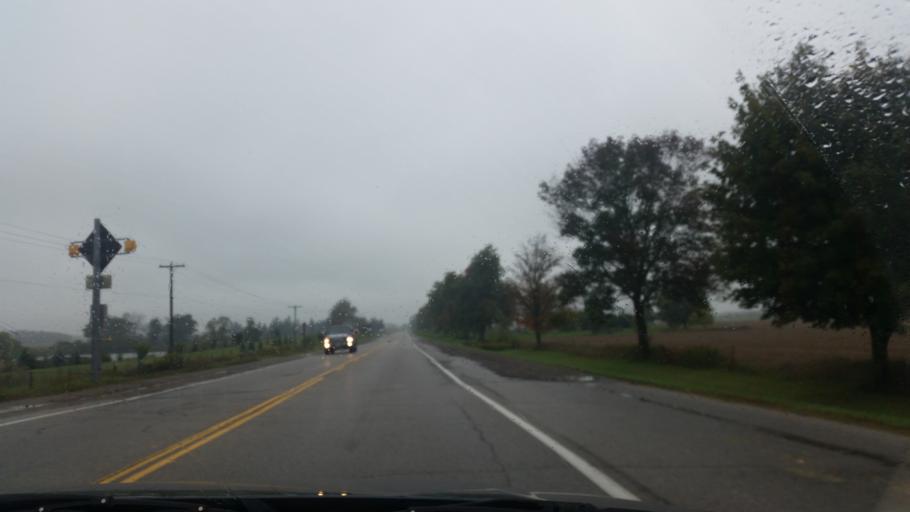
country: CA
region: Ontario
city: Waterloo
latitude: 43.5952
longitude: -80.5095
